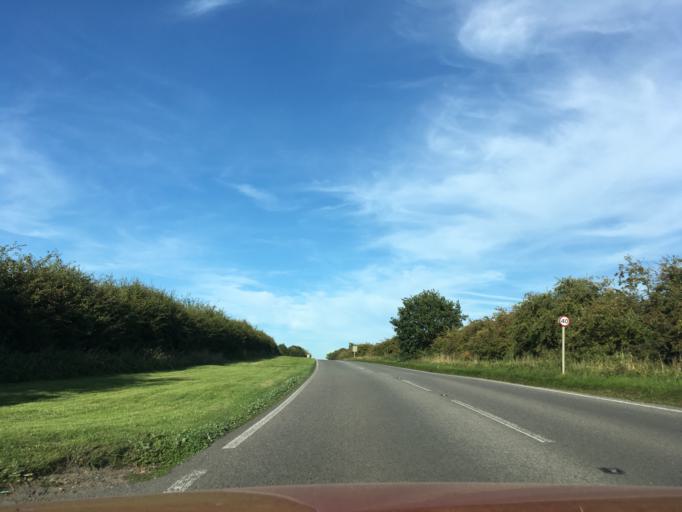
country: GB
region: England
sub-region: South Gloucestershire
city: Siston
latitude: 51.5067
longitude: -2.4677
